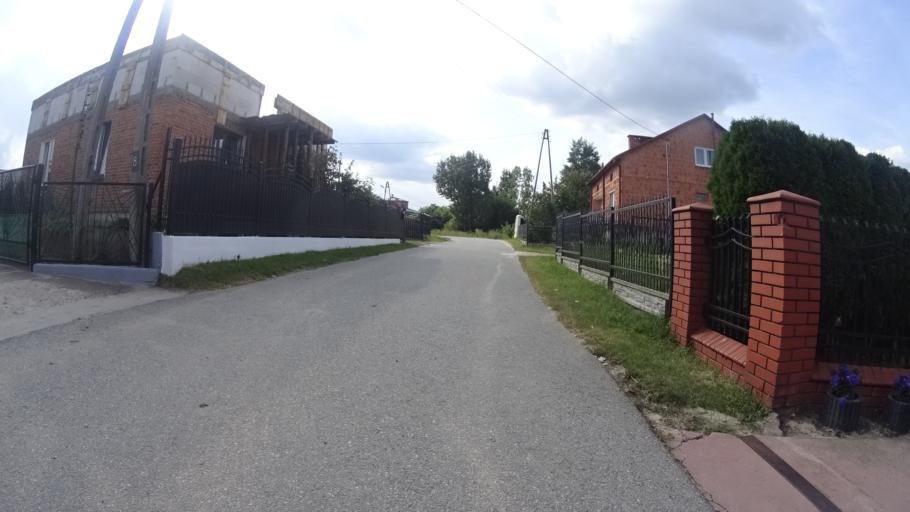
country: PL
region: Masovian Voivodeship
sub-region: Powiat grojecki
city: Mogielnica
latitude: 51.6577
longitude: 20.7583
